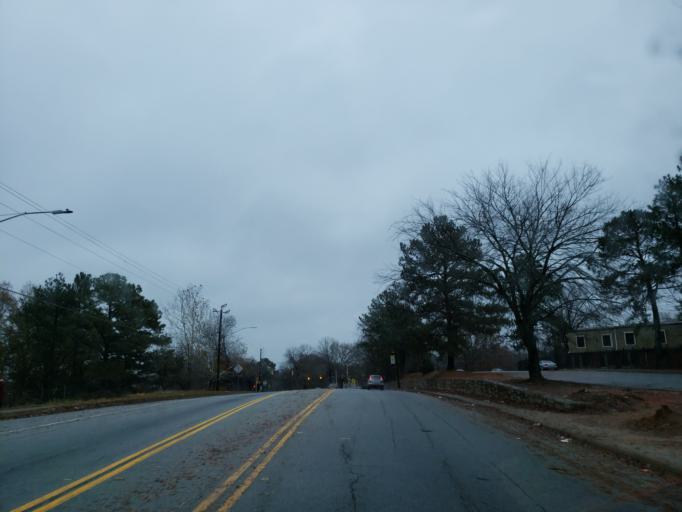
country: US
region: Georgia
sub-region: DeKalb County
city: Gresham Park
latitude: 33.7063
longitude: -84.3567
